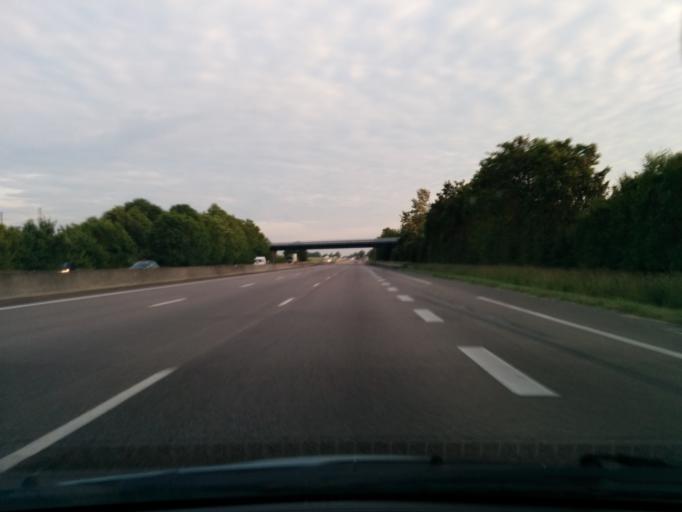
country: FR
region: Haute-Normandie
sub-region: Departement de l'Eure
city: Saint-Marcel
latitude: 49.0656
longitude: 1.4183
